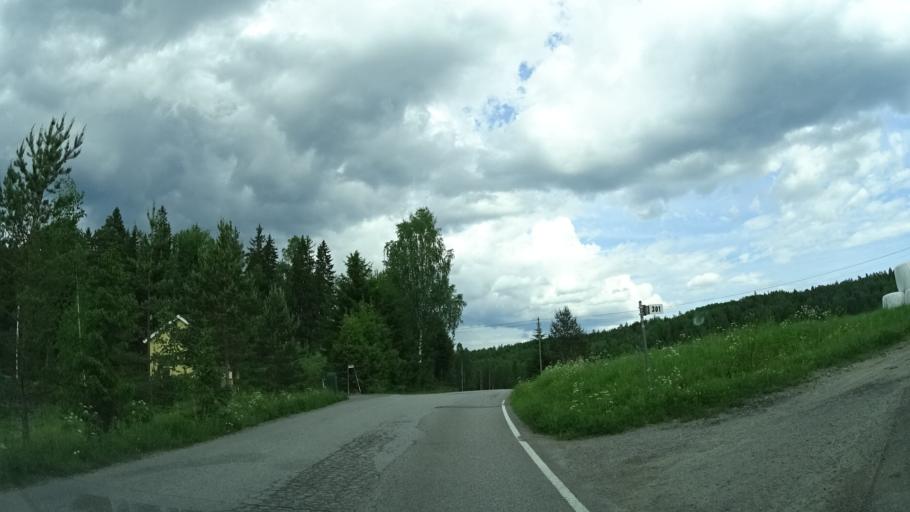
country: FI
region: Uusimaa
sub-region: Helsinki
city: Siuntio
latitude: 60.2066
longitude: 24.2360
